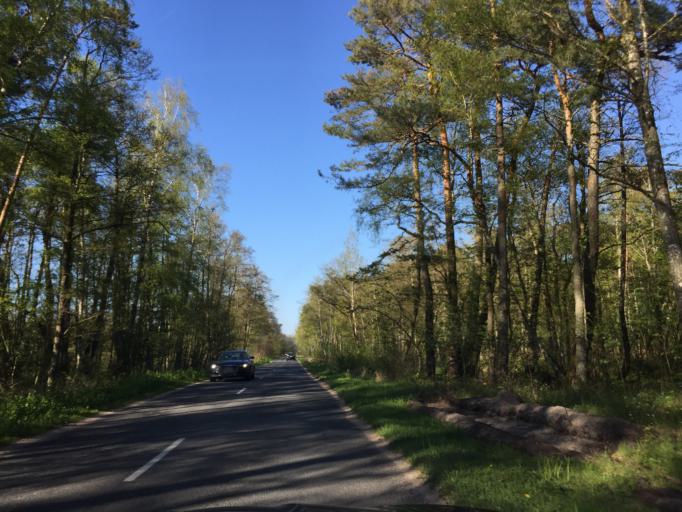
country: LT
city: Nida
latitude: 55.2102
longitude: 20.8785
